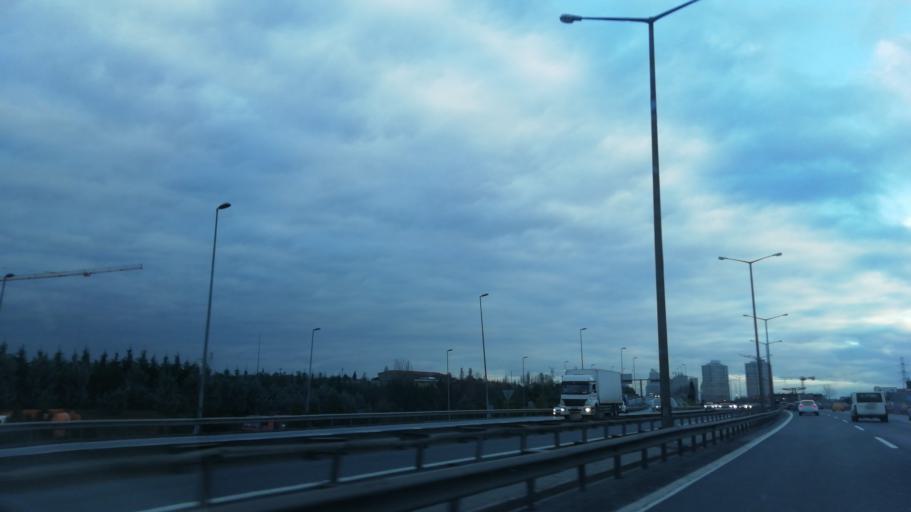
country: TR
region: Istanbul
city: Esenler
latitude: 41.0700
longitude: 28.8642
